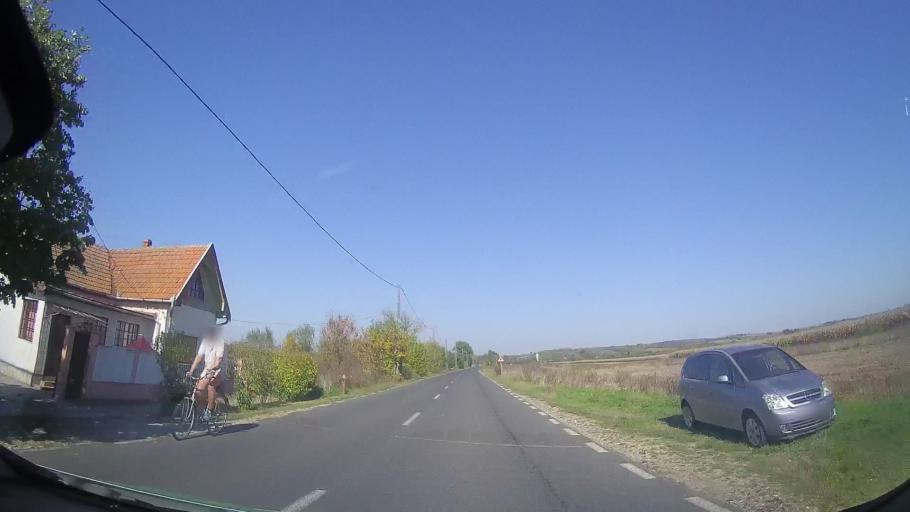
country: RO
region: Timis
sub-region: Comuna Balint
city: Balint
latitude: 45.8036
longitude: 21.8619
